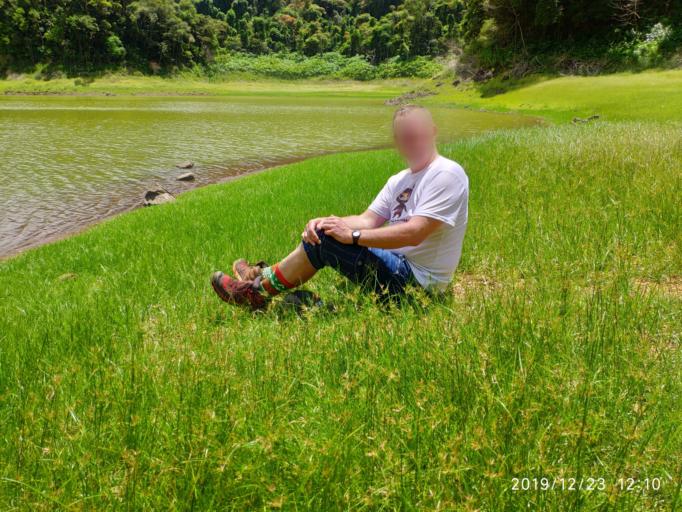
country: MG
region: Diana
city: Sadjoavato
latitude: -12.5343
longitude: 49.1762
